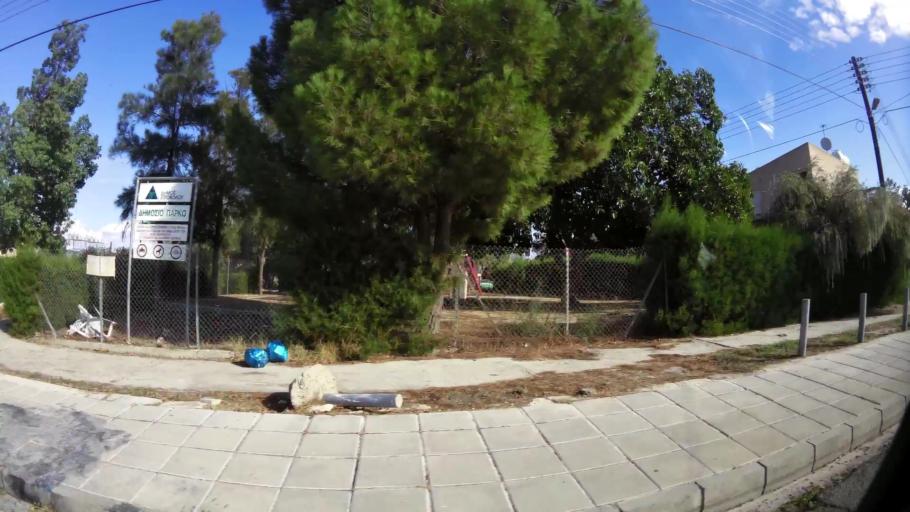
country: CY
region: Lefkosia
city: Nicosia
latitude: 35.1283
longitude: 33.3476
